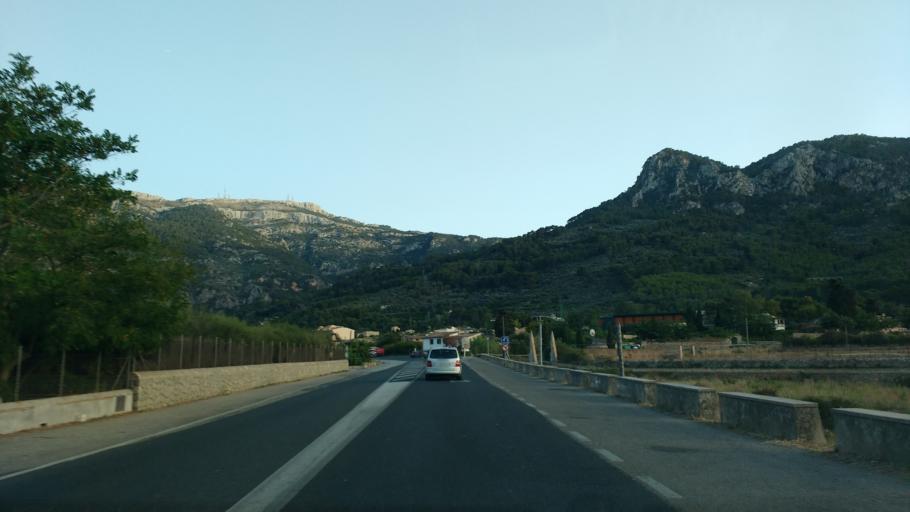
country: ES
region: Balearic Islands
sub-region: Illes Balears
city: Soller
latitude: 39.7746
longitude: 2.7055
